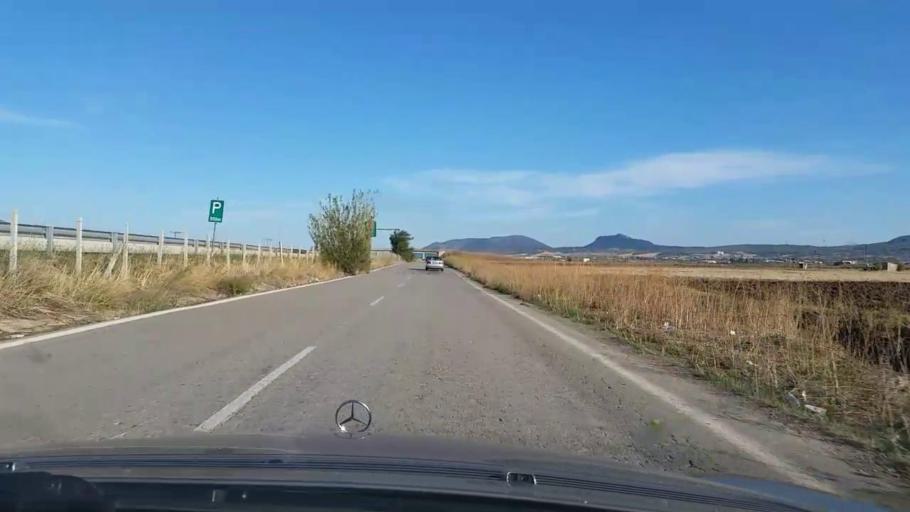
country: GR
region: Central Greece
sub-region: Nomos Voiotias
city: Thivai
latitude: 38.3689
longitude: 23.2945
